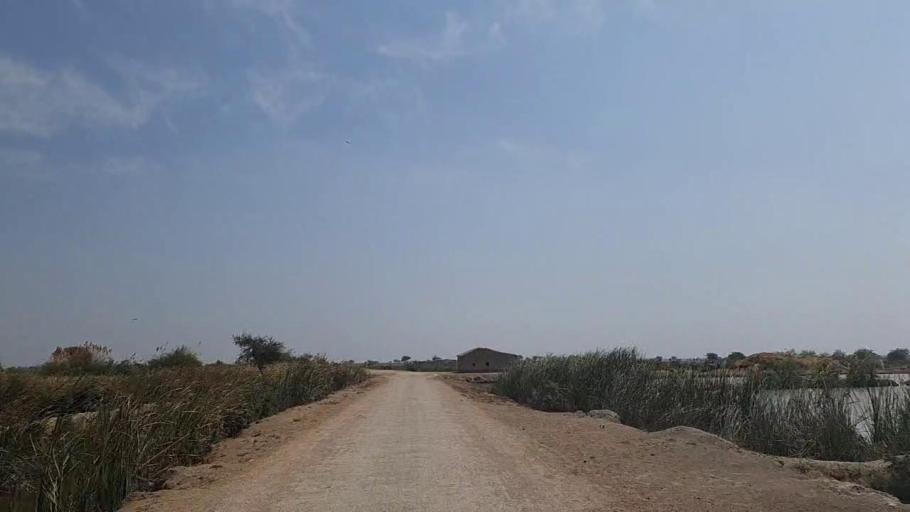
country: PK
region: Sindh
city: Mirpur Batoro
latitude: 24.5852
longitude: 68.2960
